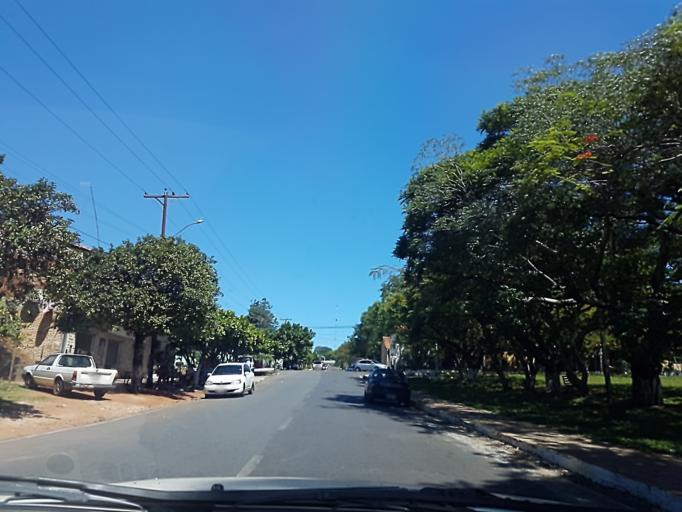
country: PY
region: Cordillera
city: Altos
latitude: -25.2625
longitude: -57.2476
